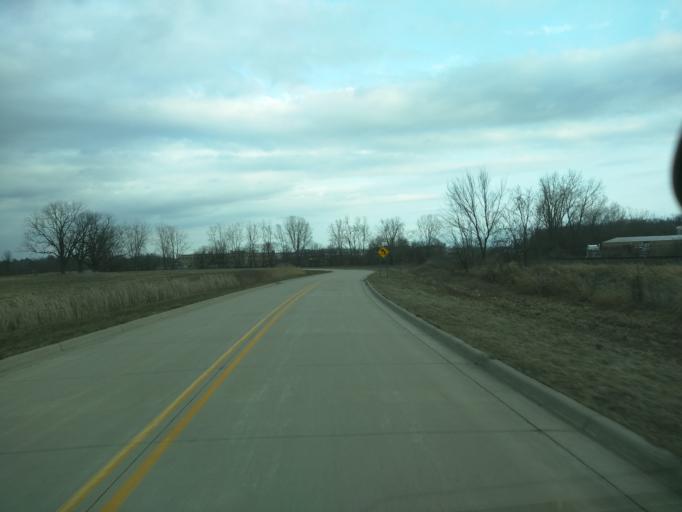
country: US
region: Michigan
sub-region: Ingham County
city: Edgemont Park
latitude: 42.7695
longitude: -84.5793
